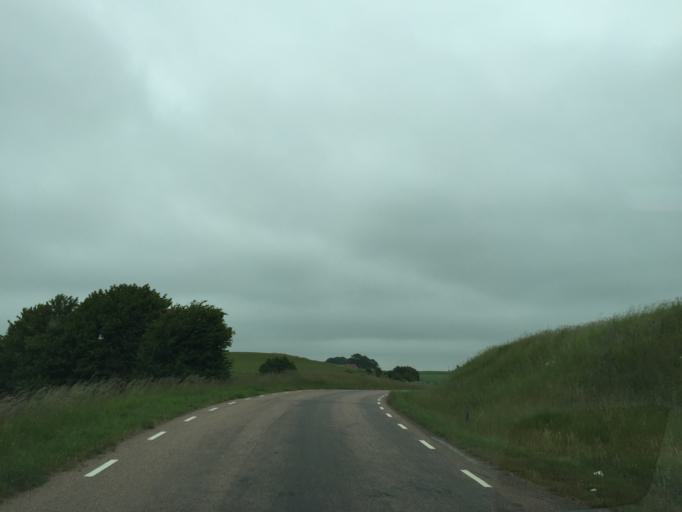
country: SE
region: Skane
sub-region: Ystads Kommun
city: Kopingebro
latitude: 55.4467
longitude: 14.0319
